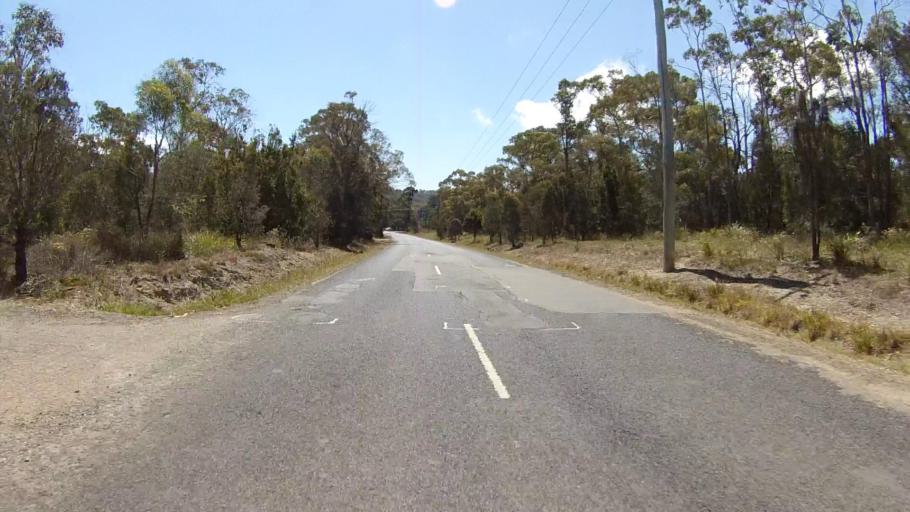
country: AU
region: Tasmania
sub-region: Clarence
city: Sandford
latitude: -42.9666
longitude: 147.4773
